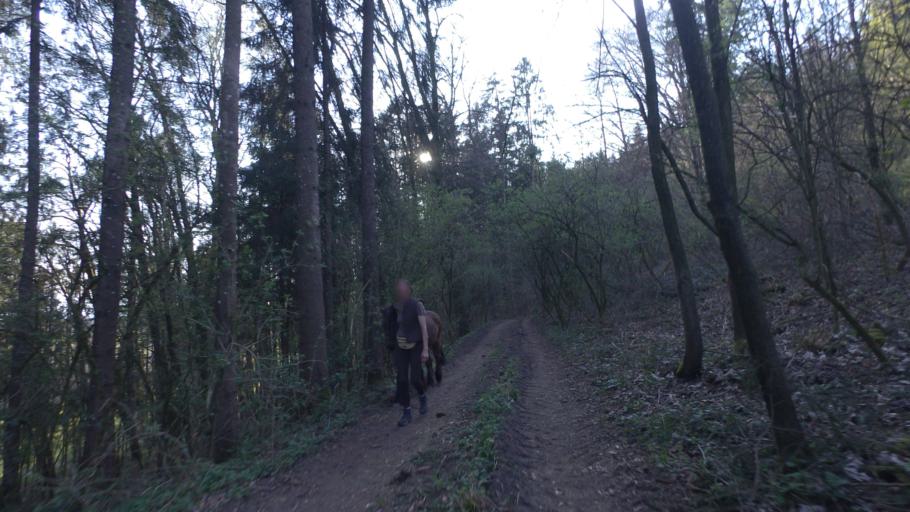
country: DE
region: Bavaria
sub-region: Upper Bavaria
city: Nussdorf
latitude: 47.9063
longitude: 12.5812
